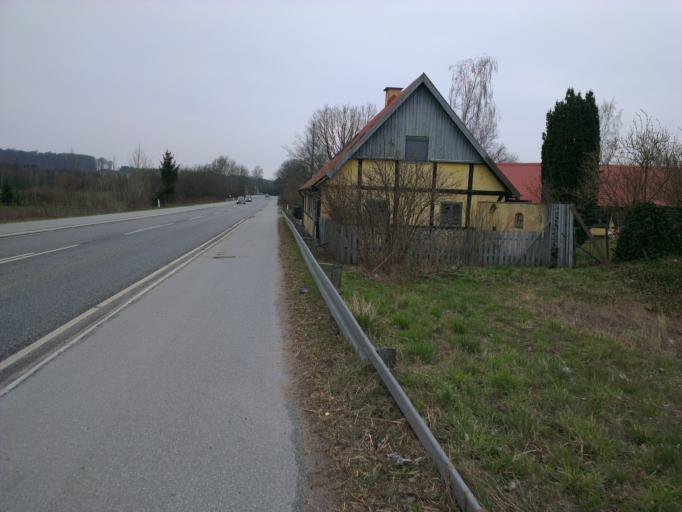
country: DK
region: Capital Region
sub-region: Frederikssund Kommune
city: Skibby
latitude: 55.7713
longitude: 11.9598
